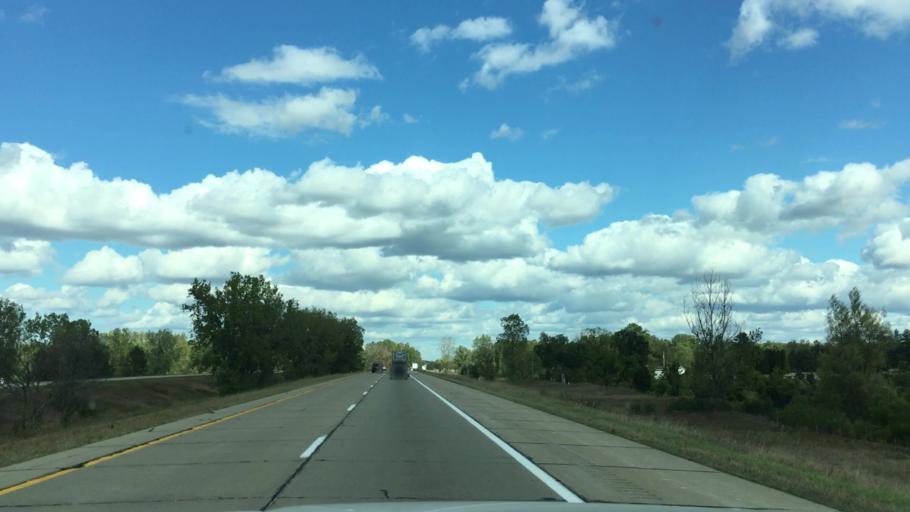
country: US
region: Michigan
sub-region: Eaton County
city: Olivet
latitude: 42.4679
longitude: -84.8985
